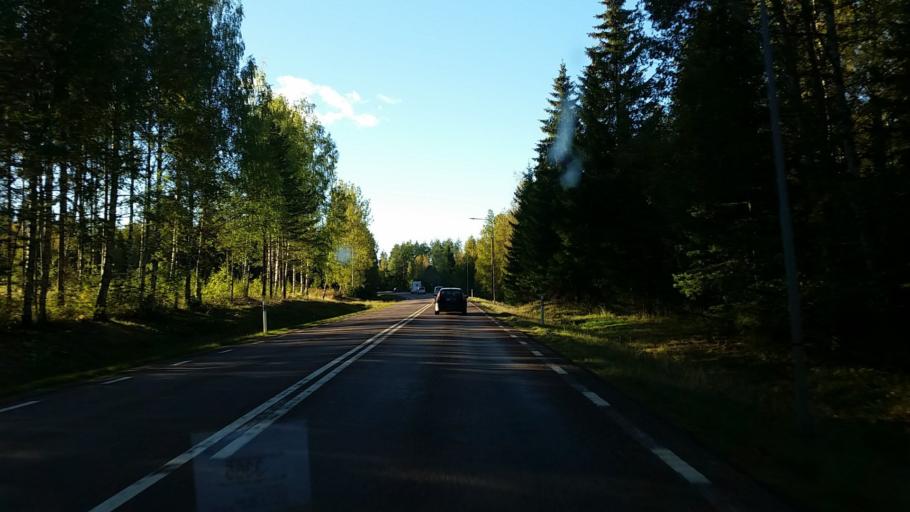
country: SE
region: Gaevleborg
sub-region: Hudiksvalls Kommun
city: Delsbo
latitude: 61.7992
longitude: 16.4956
